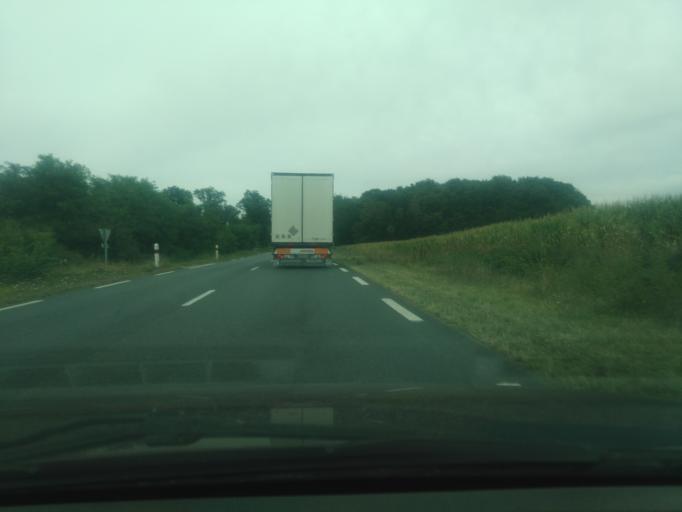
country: FR
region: Poitou-Charentes
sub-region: Departement de la Vienne
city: Lavoux
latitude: 46.5608
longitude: 0.5381
